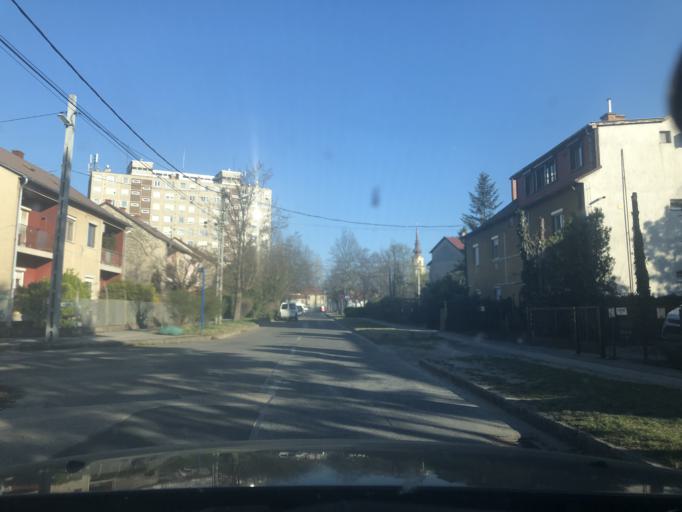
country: HU
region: Pest
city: Dunakeszi
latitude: 47.6458
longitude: 19.1279
